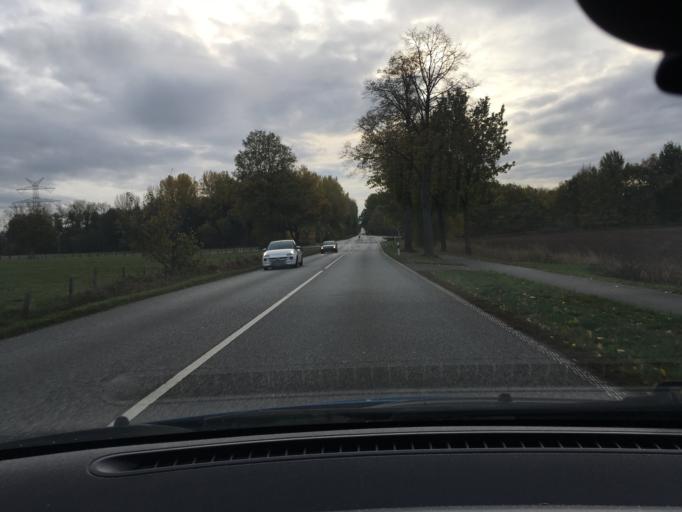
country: DE
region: Schleswig-Holstein
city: Sahms
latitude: 53.5326
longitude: 10.5209
